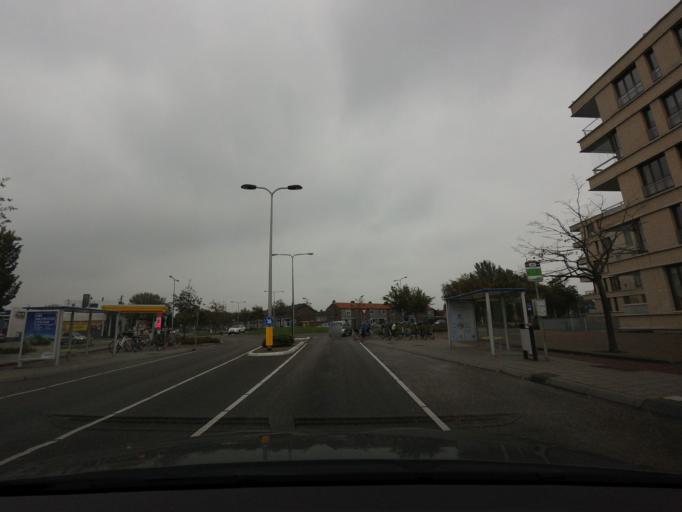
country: NL
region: South Holland
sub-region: Gemeente Noordwijk
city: Noordwijk-Binnen
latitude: 52.2414
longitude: 4.4458
